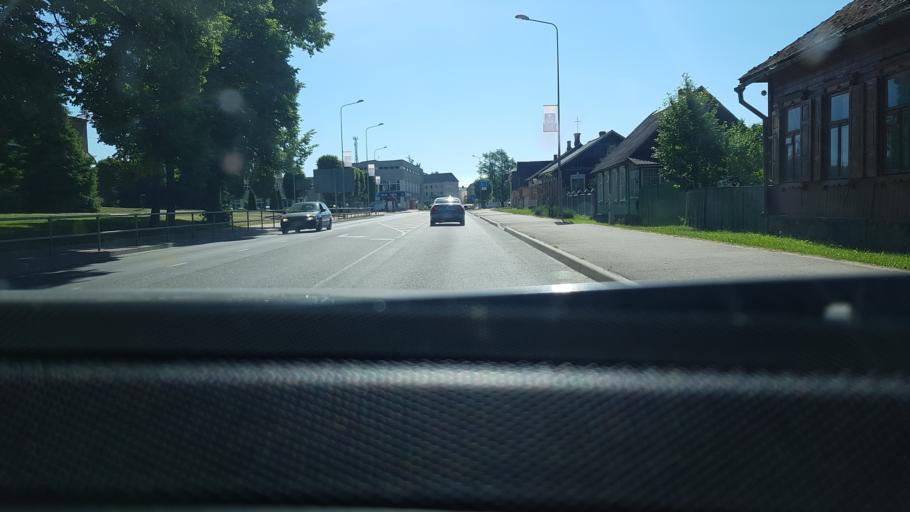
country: LV
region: Kraslavas Rajons
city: Kraslava
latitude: 55.8976
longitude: 27.1590
